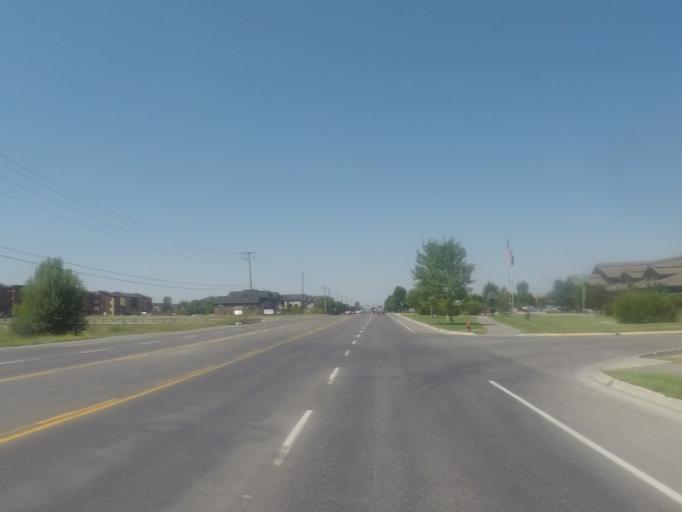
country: US
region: Montana
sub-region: Gallatin County
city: Bozeman
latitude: 45.6931
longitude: -111.0511
